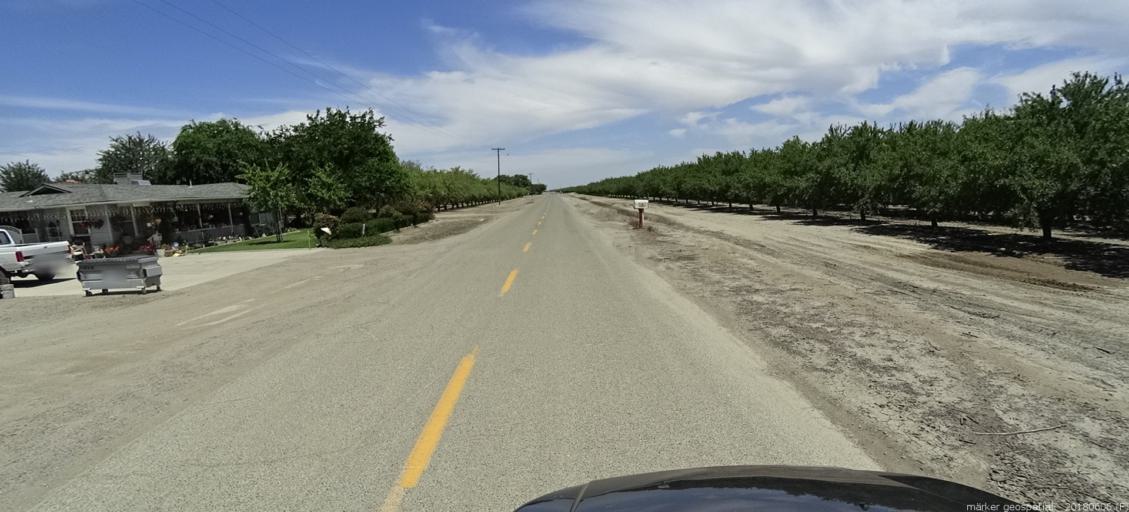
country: US
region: California
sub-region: Fresno County
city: Firebaugh
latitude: 36.8479
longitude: -120.3910
